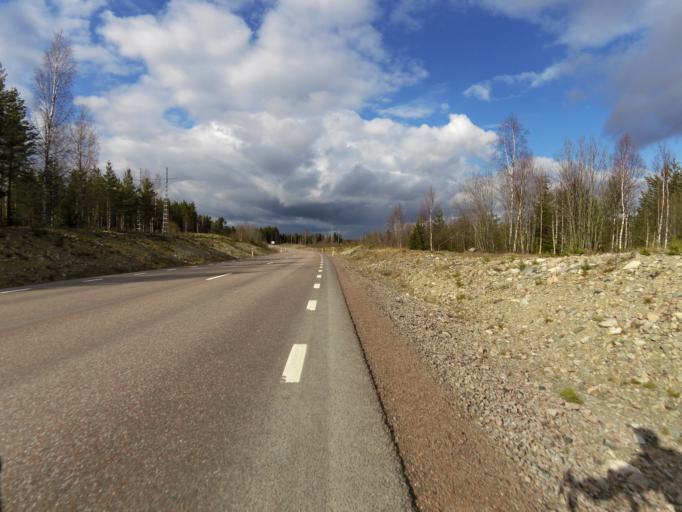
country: SE
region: Gaevleborg
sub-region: Hofors Kommun
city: Hofors
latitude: 60.4864
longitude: 16.4442
